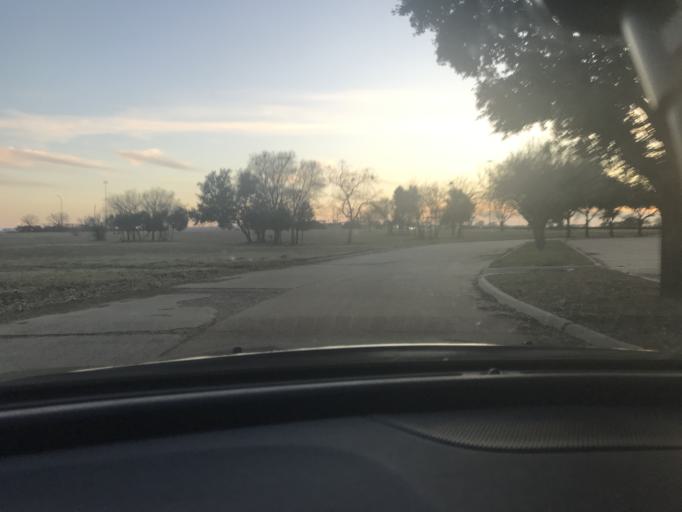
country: US
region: Texas
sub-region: Tarrant County
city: Arlington
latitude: 32.7639
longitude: -97.1003
